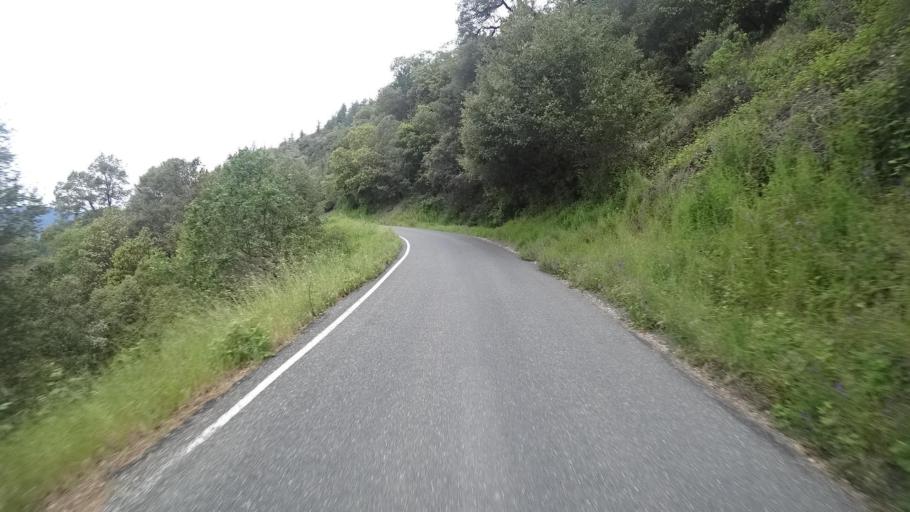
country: US
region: California
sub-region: Humboldt County
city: Willow Creek
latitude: 40.9489
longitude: -123.6120
